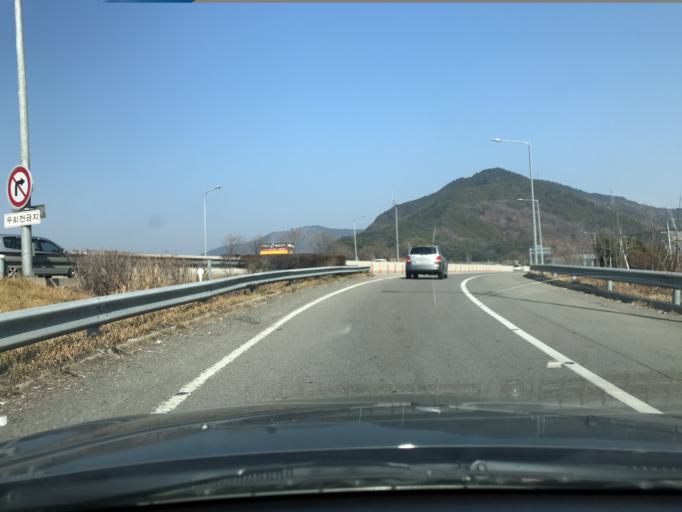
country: KR
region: Daegu
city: Hwawon
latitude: 35.7039
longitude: 128.4374
